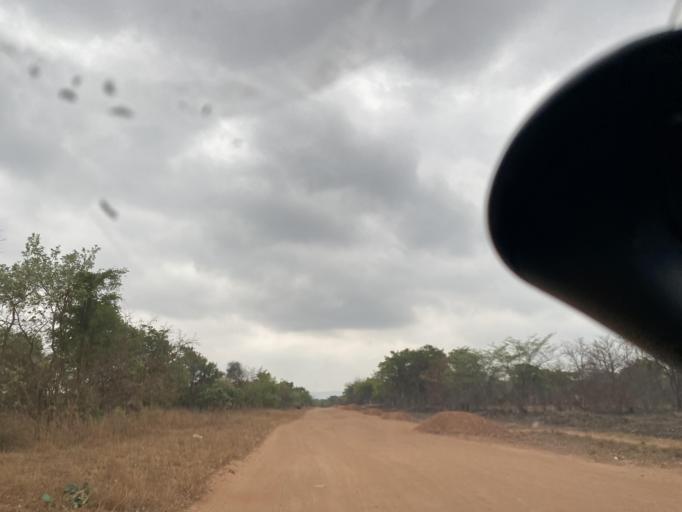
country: ZM
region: Lusaka
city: Chongwe
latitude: -15.2716
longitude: 28.7313
